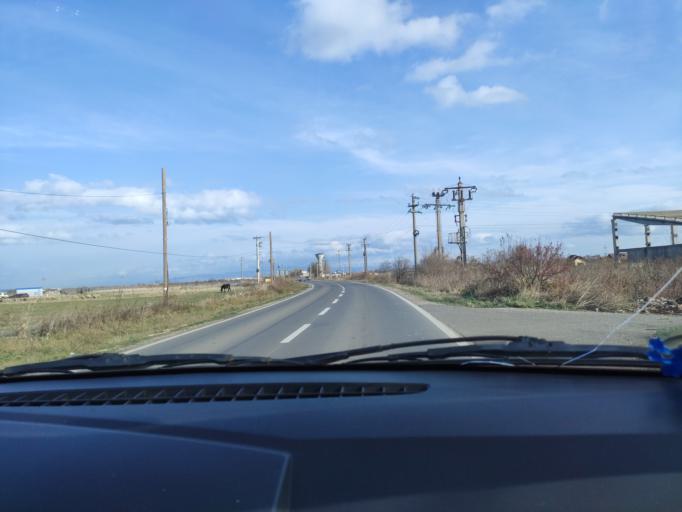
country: RO
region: Brasov
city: Codlea
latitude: 45.7101
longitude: 25.4622
